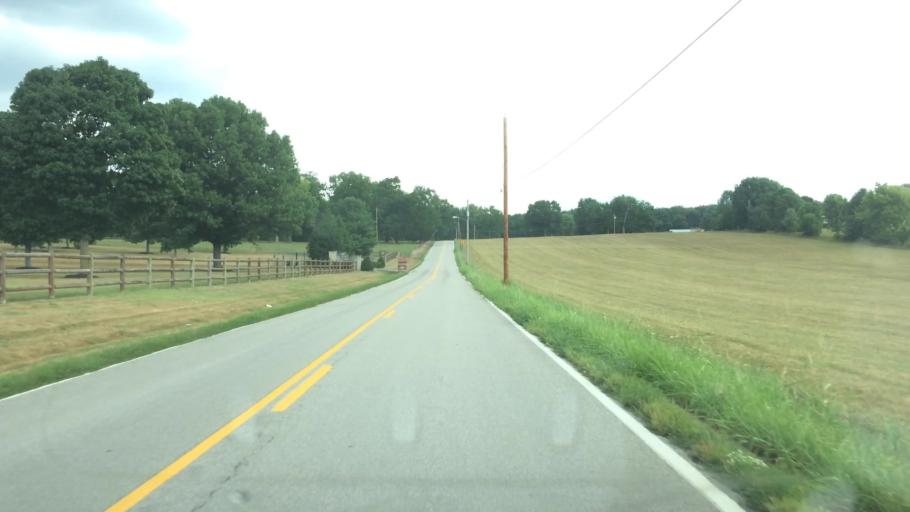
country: US
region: Missouri
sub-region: Greene County
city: Strafford
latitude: 37.1866
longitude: -93.1846
